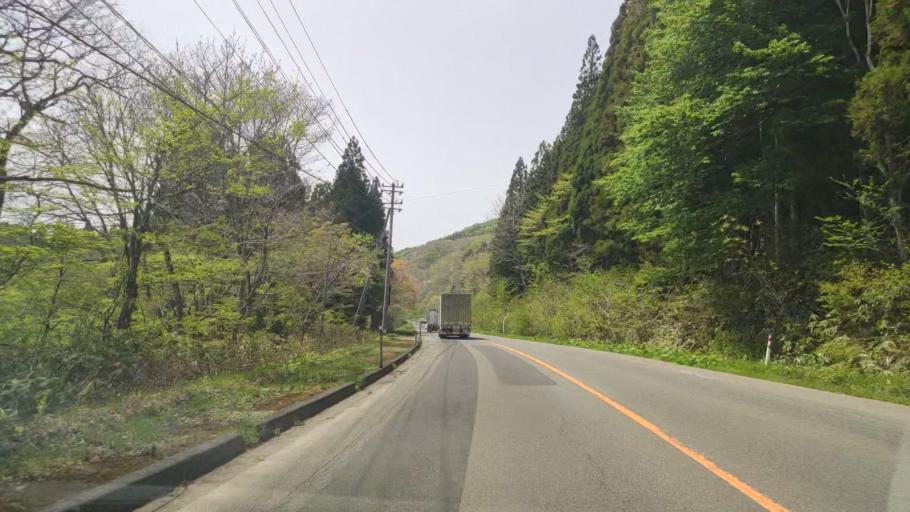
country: JP
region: Aomori
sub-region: Misawa Shi
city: Inuotose
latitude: 40.7913
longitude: 141.0948
